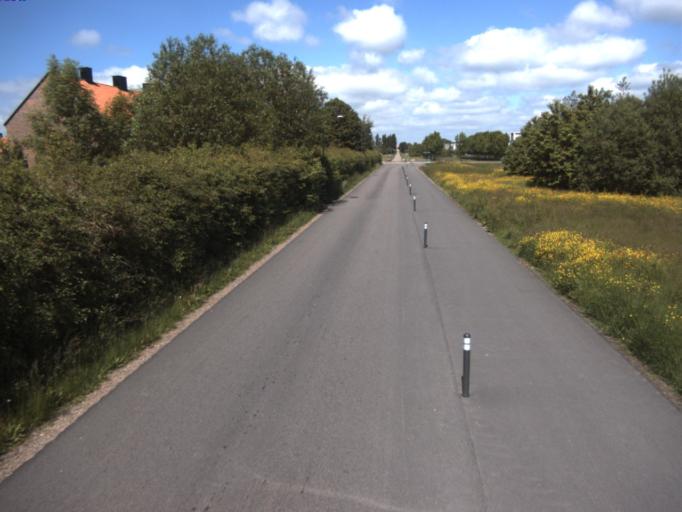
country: SE
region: Skane
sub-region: Helsingborg
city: Helsingborg
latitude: 56.0807
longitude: 12.6928
